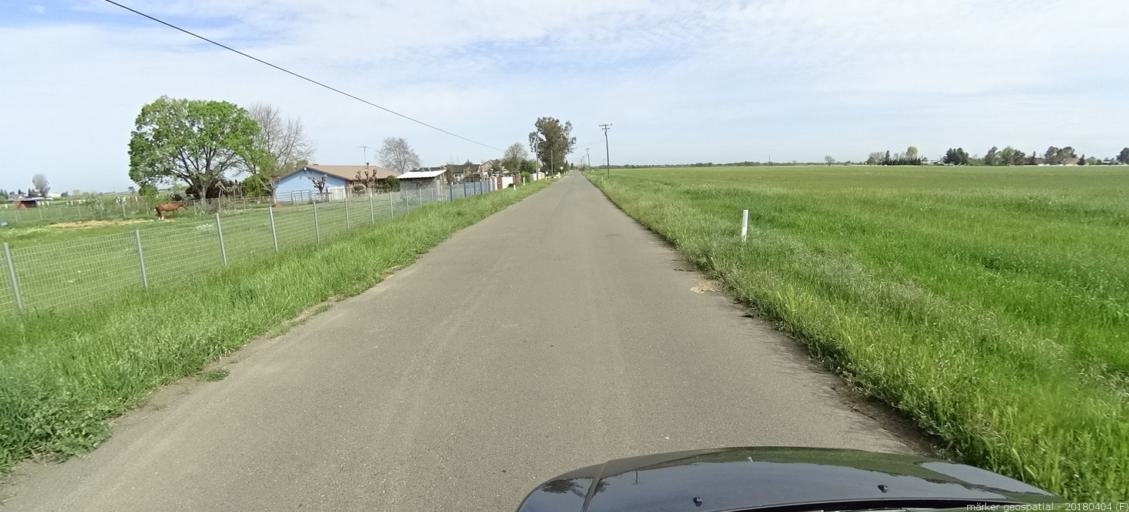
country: US
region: California
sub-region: Sacramento County
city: Herald
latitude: 38.2917
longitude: -121.2772
